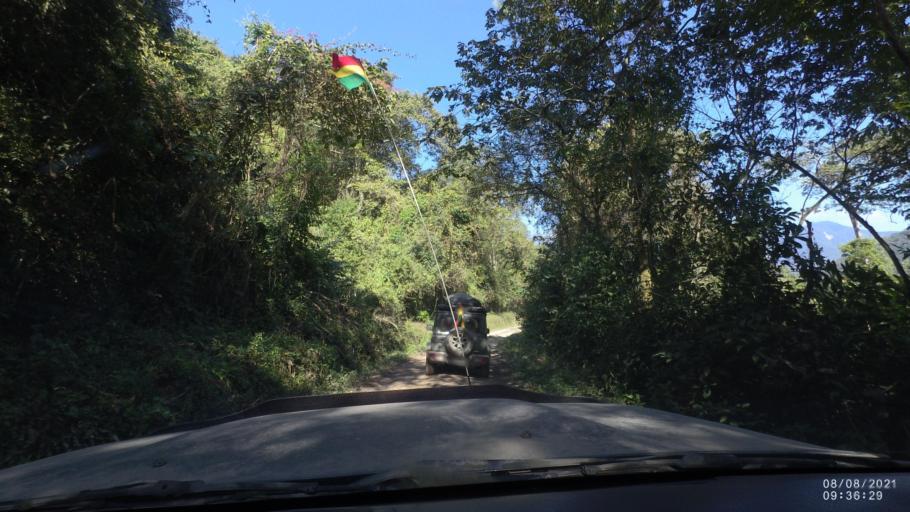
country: BO
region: La Paz
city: Quime
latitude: -16.5943
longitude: -66.7069
